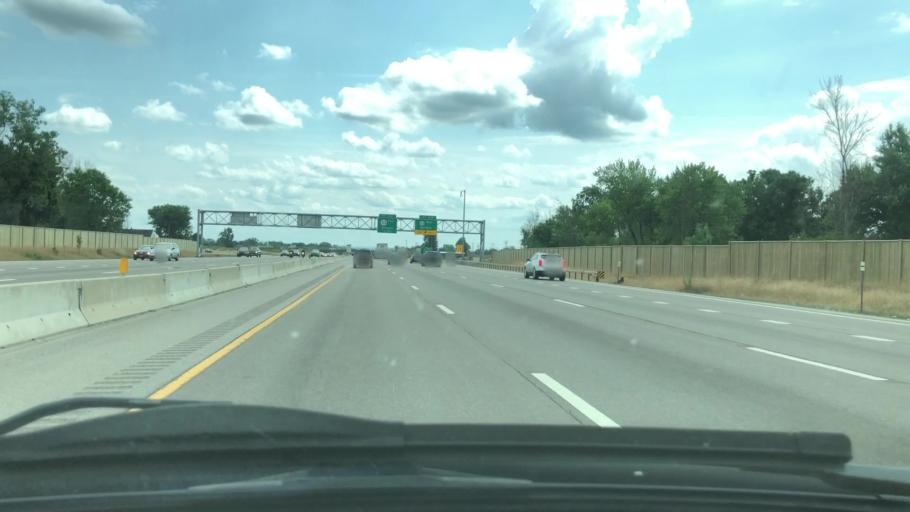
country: US
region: New York
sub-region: Erie County
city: Cheektowaga
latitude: 42.9380
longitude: -78.7664
